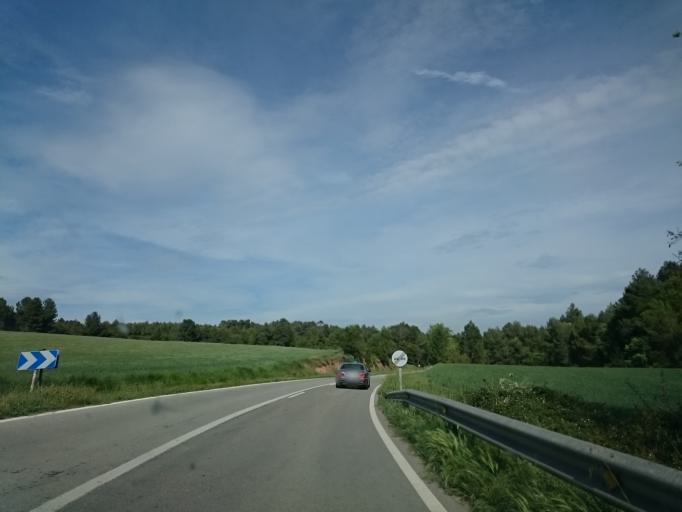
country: ES
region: Catalonia
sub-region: Provincia de Barcelona
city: Jorba
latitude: 41.5815
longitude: 1.5519
